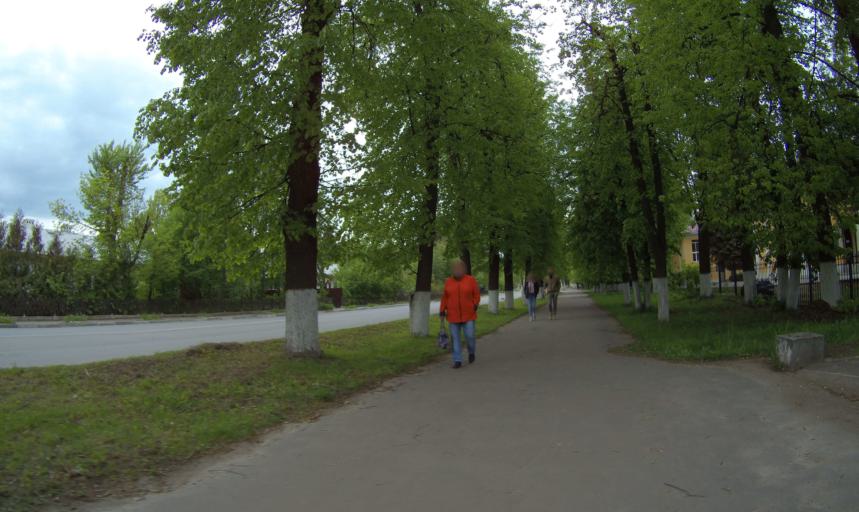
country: RU
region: Moskovskaya
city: Kolomna
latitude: 55.0725
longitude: 38.8027
